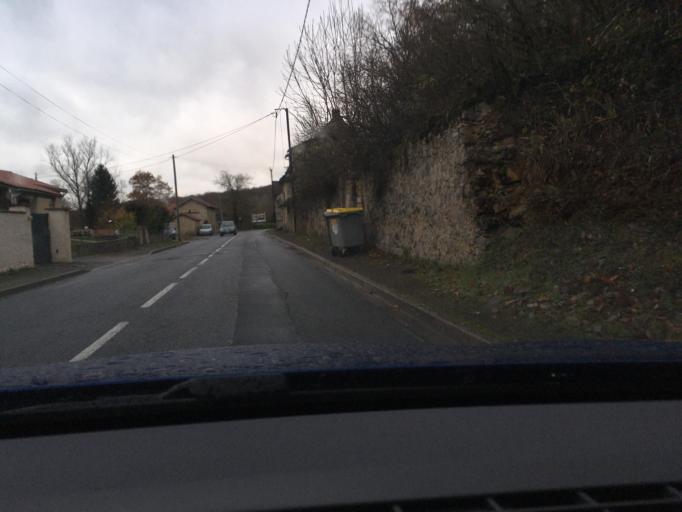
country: FR
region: Midi-Pyrenees
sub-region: Departement de l'Aveyron
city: Villefranche-de-Rouergue
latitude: 44.3626
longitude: 2.0206
